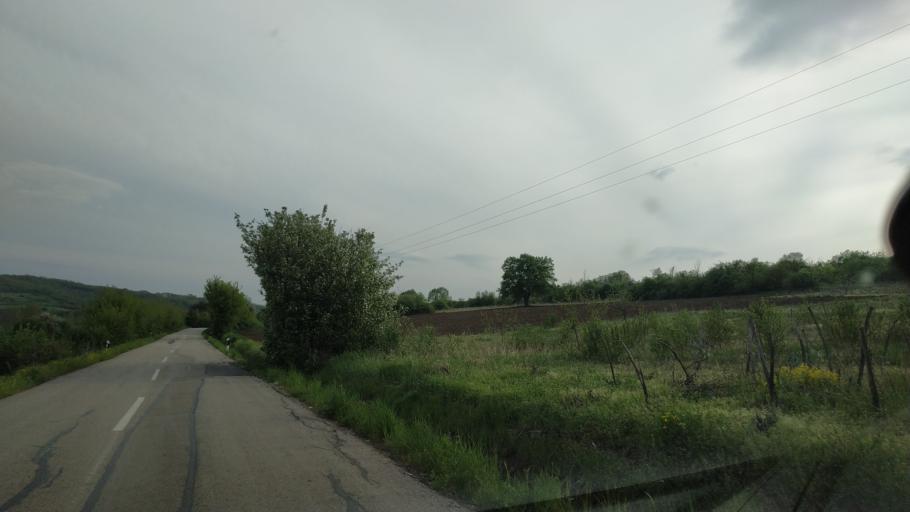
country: RS
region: Central Serbia
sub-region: Zajecarski Okrug
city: Soko Banja
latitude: 43.5104
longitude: 21.8430
